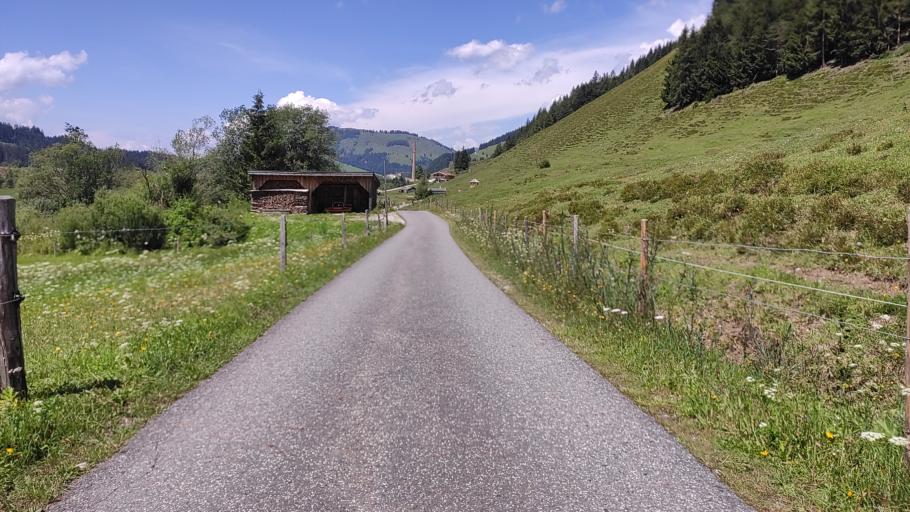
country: AT
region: Tyrol
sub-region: Politischer Bezirk Kitzbuhel
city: Hochfilzen
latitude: 47.4599
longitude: 12.6484
